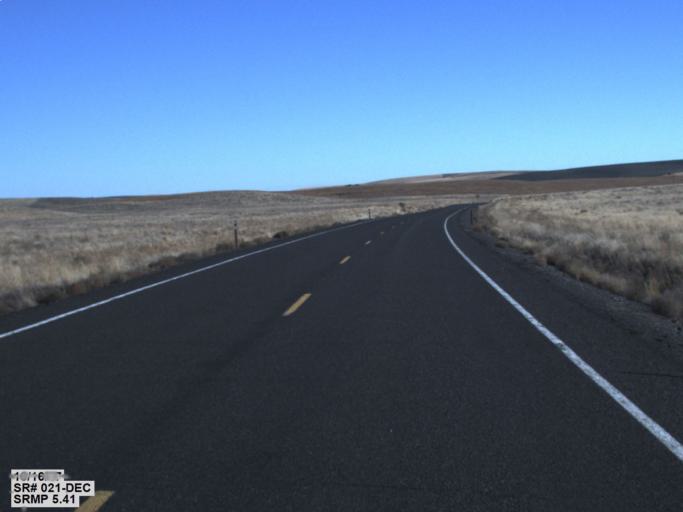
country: US
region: Washington
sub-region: Franklin County
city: Connell
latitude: 46.7107
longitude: -118.5369
